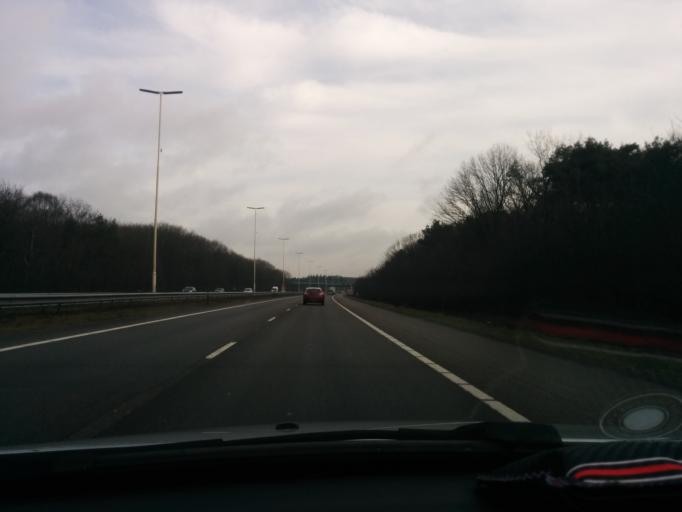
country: NL
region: North Holland
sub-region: Gemeente Hilversum
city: Hilversum
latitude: 52.1991
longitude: 5.1908
